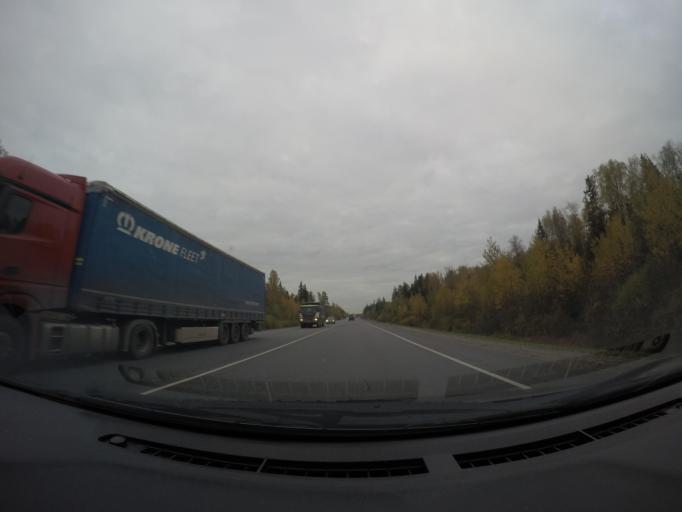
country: RU
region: Moskovskaya
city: Fryazevo
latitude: 55.7105
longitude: 38.4274
